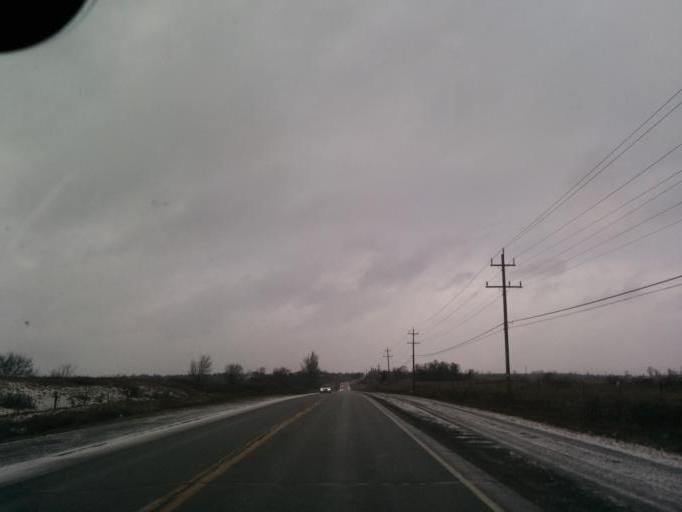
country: CA
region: Ontario
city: Orangeville
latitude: 43.8459
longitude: -80.0124
